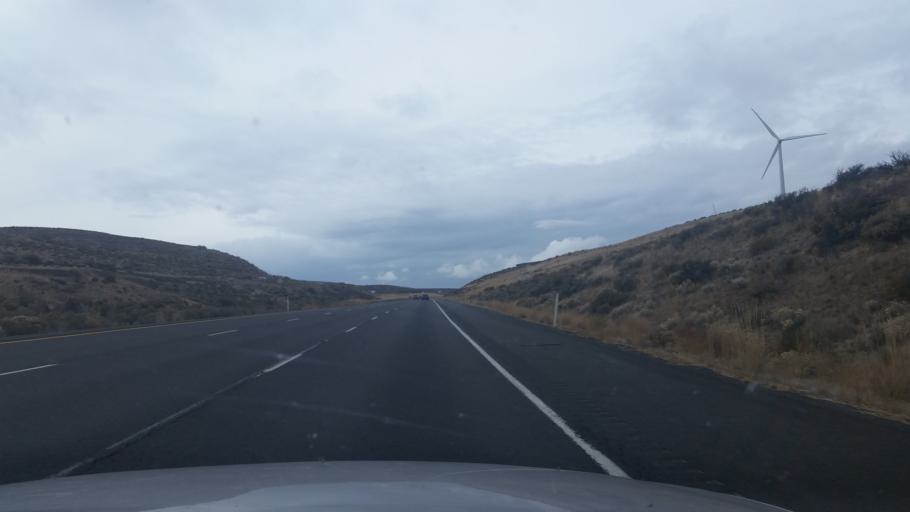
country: US
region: Washington
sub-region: Kittitas County
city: Kittitas
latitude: 46.9442
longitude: -120.1697
